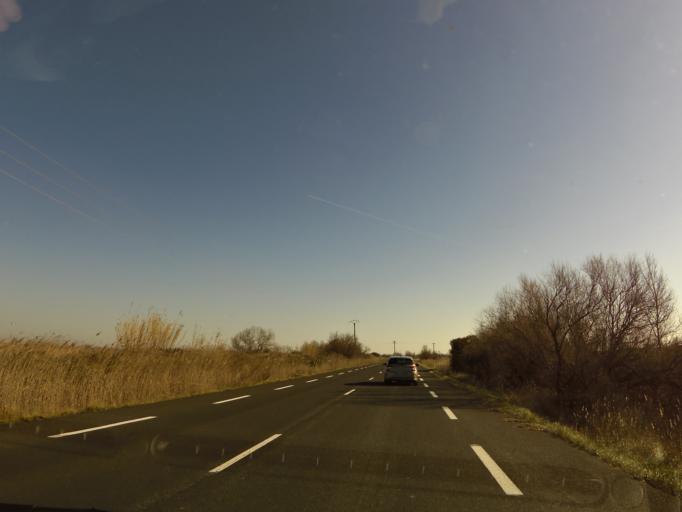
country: FR
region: Languedoc-Roussillon
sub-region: Departement du Gard
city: Aigues-Mortes
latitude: 43.5576
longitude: 4.3197
